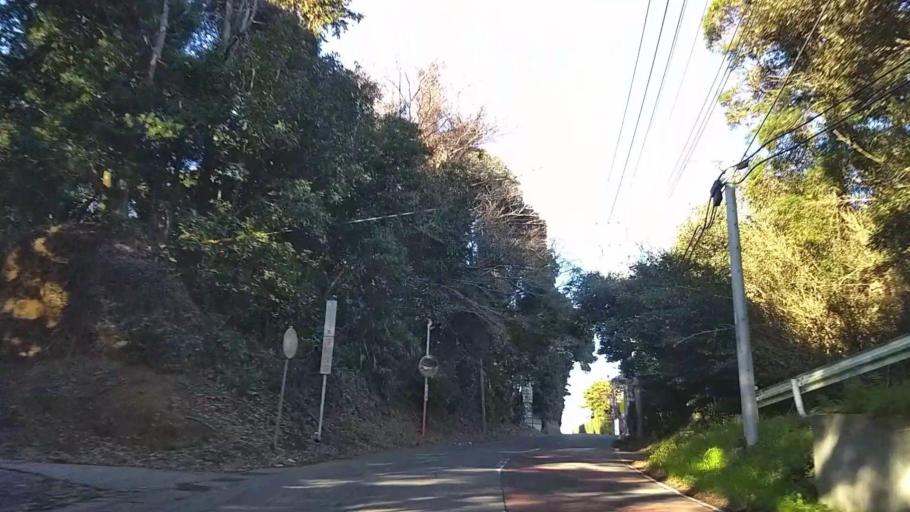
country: JP
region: Chiba
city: Asahi
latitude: 35.7209
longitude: 140.7348
